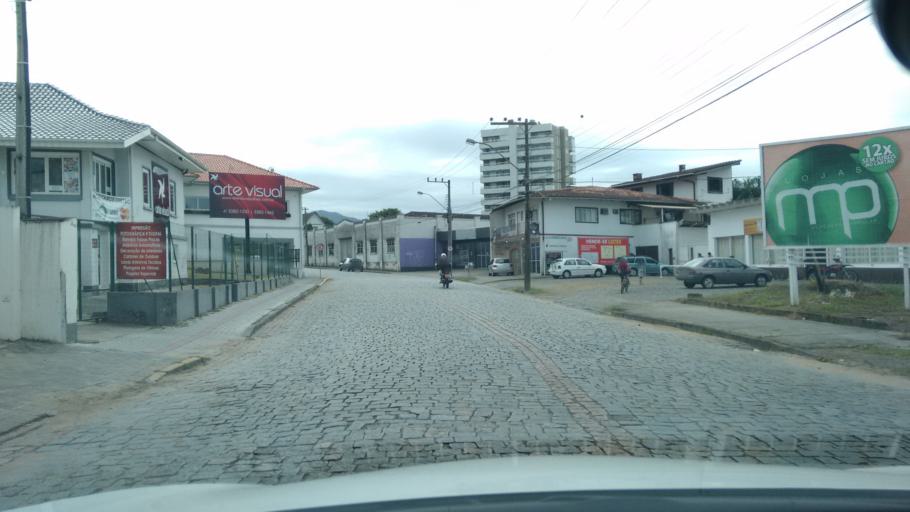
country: BR
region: Santa Catarina
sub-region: Timbo
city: Timbo
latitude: -26.8281
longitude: -49.2683
